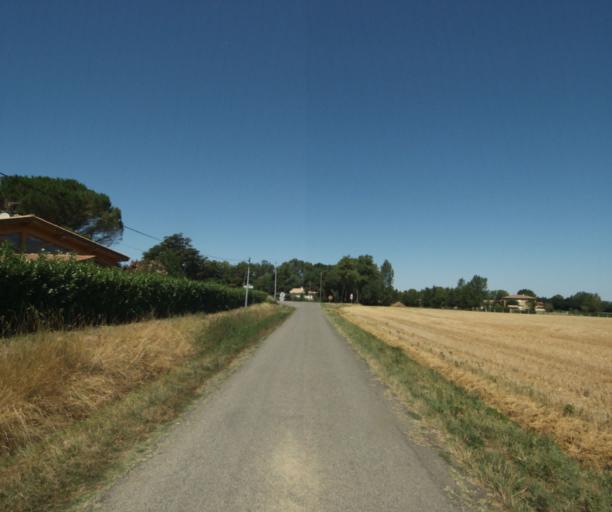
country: FR
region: Midi-Pyrenees
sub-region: Departement de la Haute-Garonne
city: Saint-Felix-Lauragais
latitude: 43.4594
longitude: 1.9283
